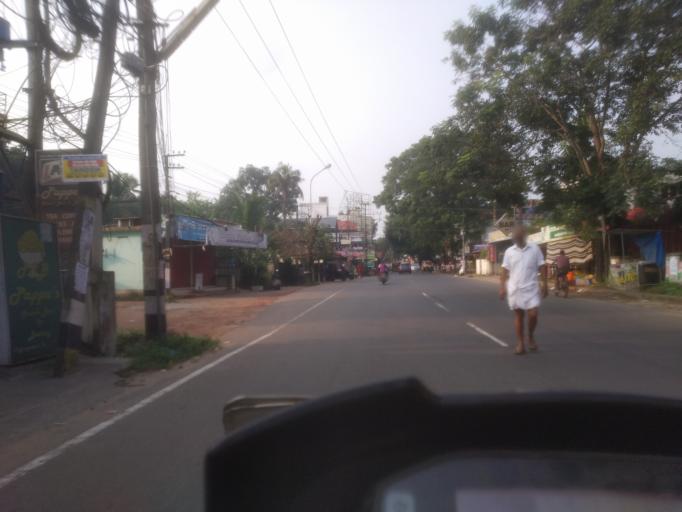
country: IN
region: Kerala
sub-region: Alappuzha
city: Arukutti
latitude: 9.9133
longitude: 76.3638
